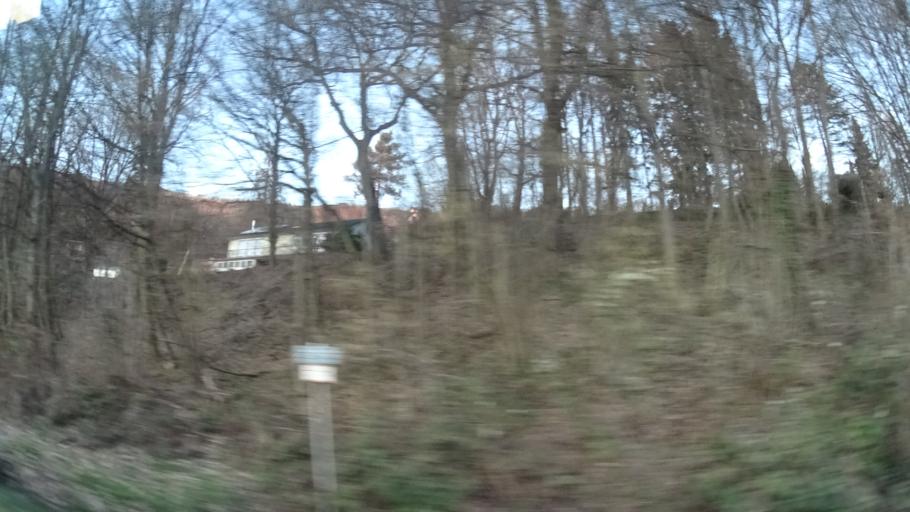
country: DE
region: Bavaria
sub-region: Regierungsbezirk Unterfranken
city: Mombris
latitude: 50.1007
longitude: 9.1204
